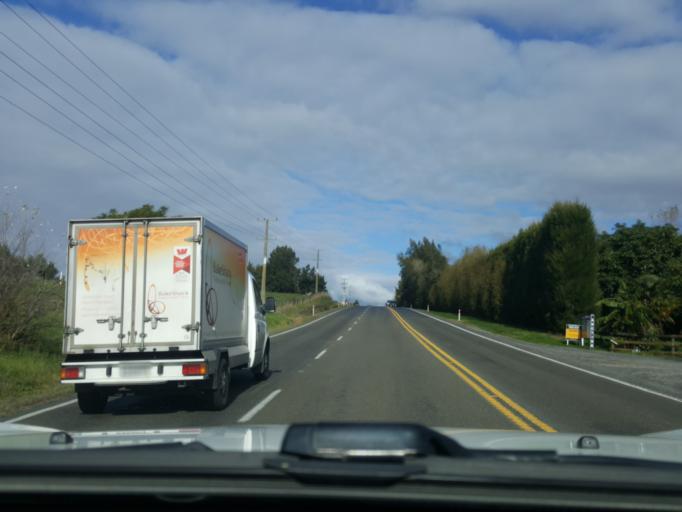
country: NZ
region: Bay of Plenty
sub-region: Tauranga City
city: Tauranga
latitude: -37.6725
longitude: 176.0223
